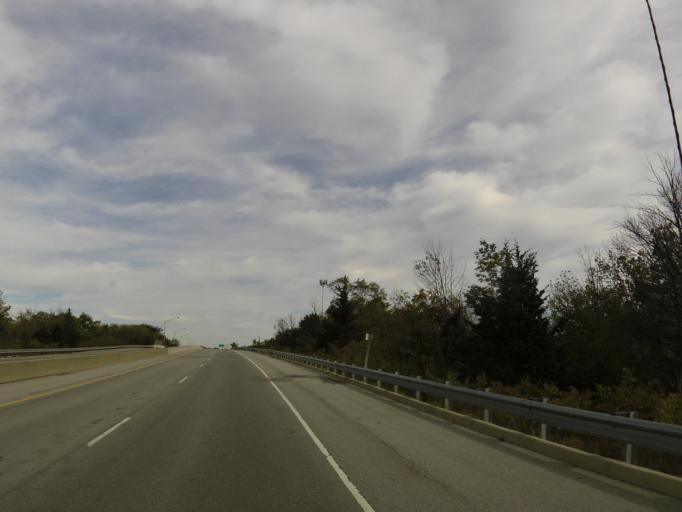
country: US
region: Indiana
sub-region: Marion County
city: Warren Park
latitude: 39.7581
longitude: -86.0419
